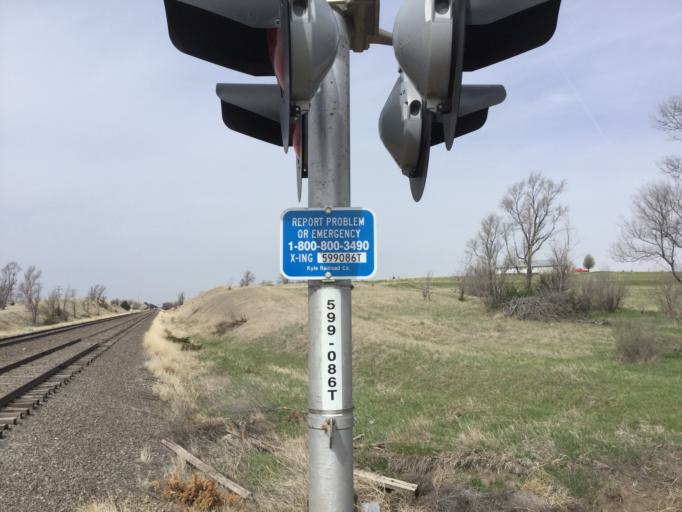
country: US
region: Kansas
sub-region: Norton County
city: Norton
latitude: 39.8255
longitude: -99.9078
